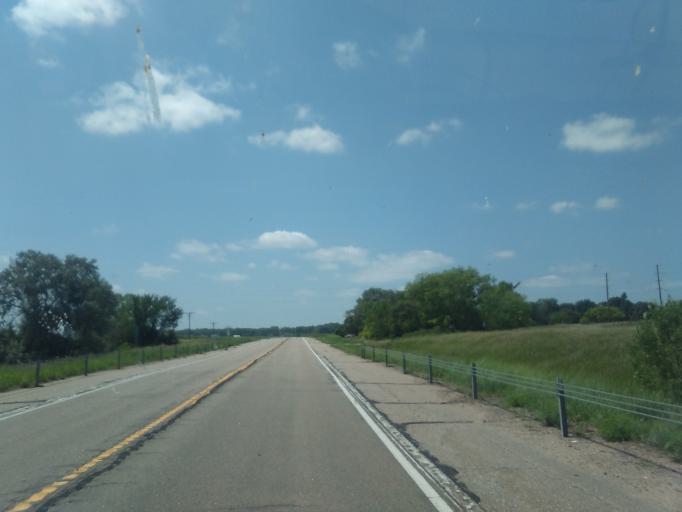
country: US
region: Nebraska
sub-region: Gosper County
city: Elwood
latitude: 40.6845
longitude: -99.8110
